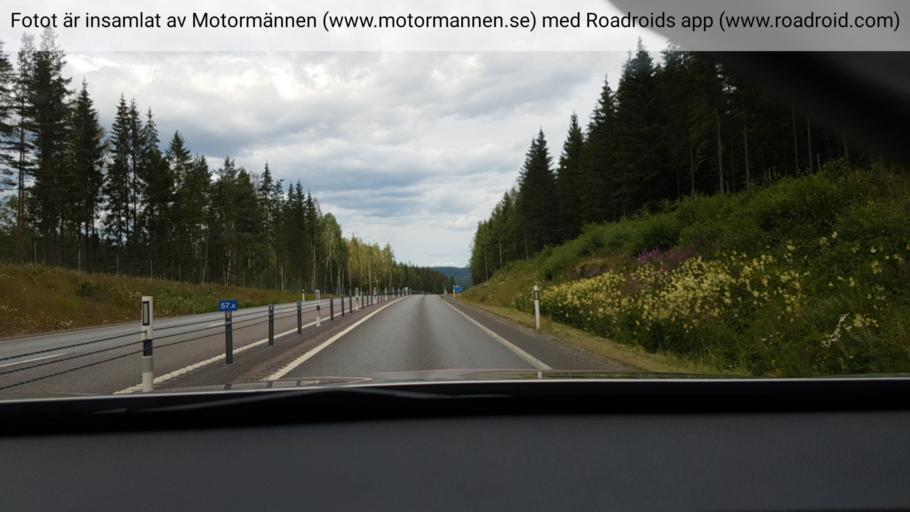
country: SE
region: Vaermland
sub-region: Arvika Kommun
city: Arvika
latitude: 59.6531
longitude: 12.7560
